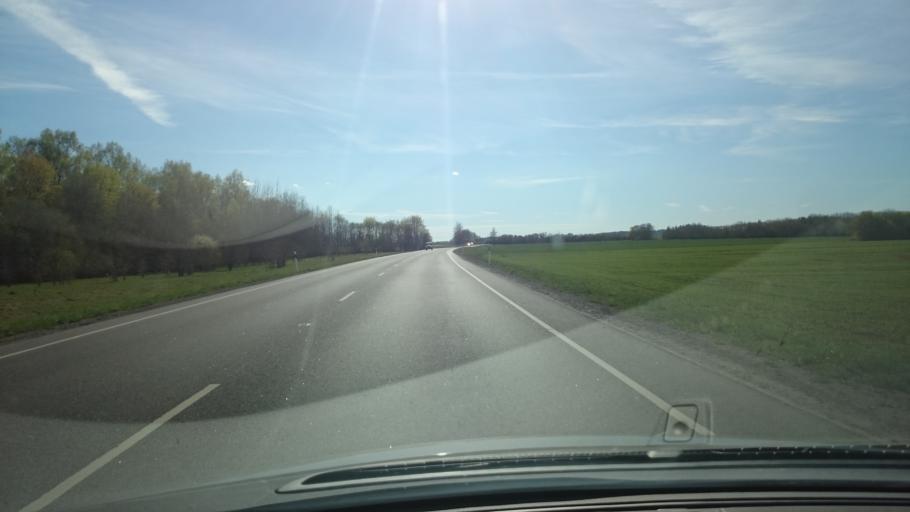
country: EE
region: Laeaene-Virumaa
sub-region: Kadrina vald
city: Kadrina
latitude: 59.3522
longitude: 26.1588
